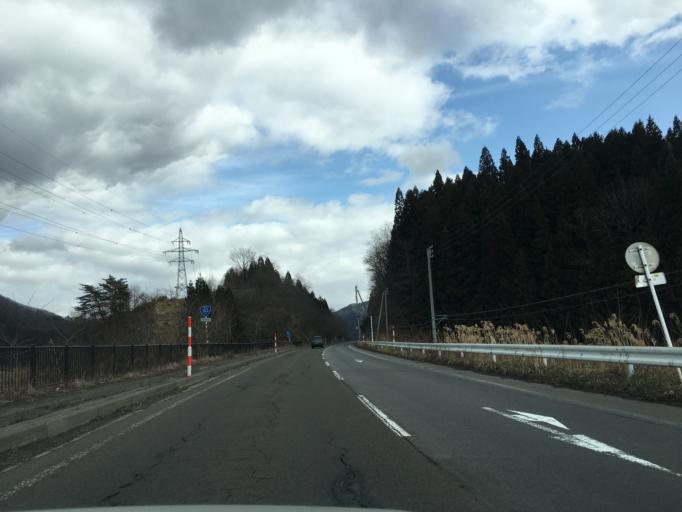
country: JP
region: Akita
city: Odate
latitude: 40.2221
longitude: 140.6542
